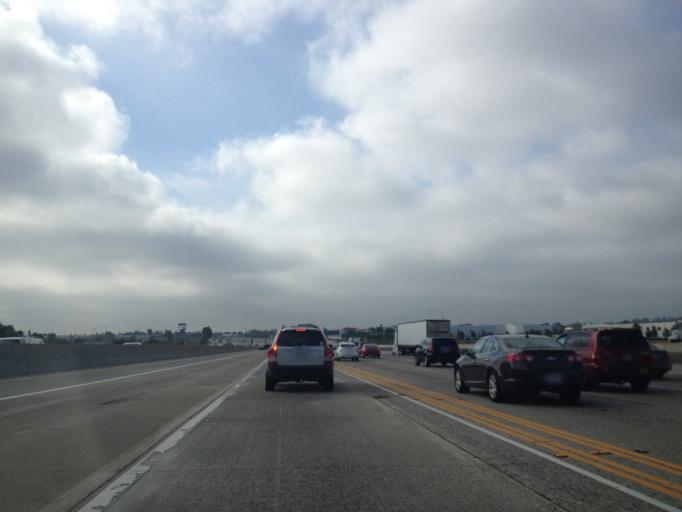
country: US
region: California
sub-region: Orange County
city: Laguna Woods
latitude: 33.6382
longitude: -117.7302
